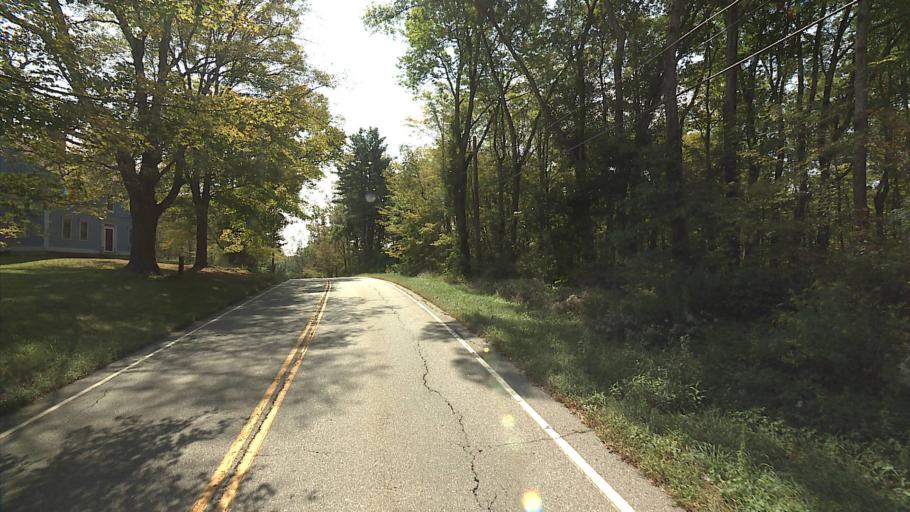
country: US
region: Connecticut
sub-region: Windham County
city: Plainfield Village
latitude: 41.6906
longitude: -71.9690
